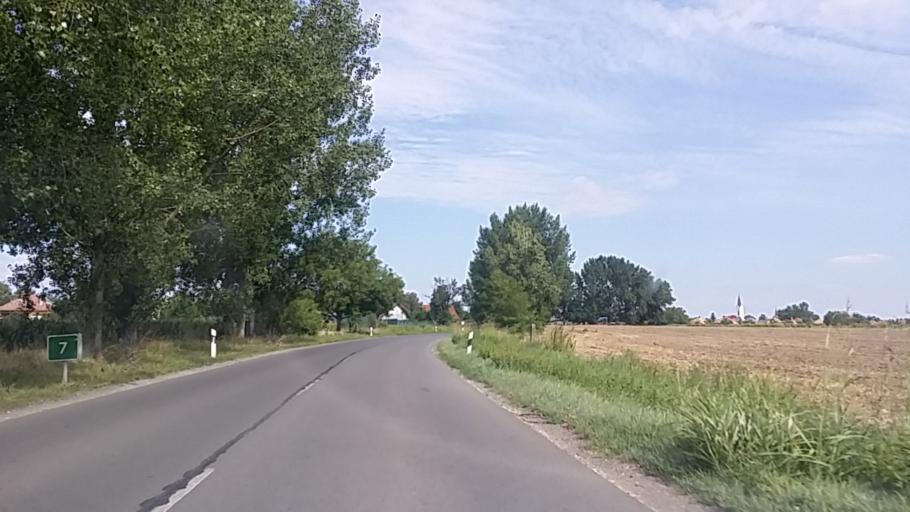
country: HU
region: Tolna
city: Dombovar
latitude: 46.3239
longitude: 18.1301
